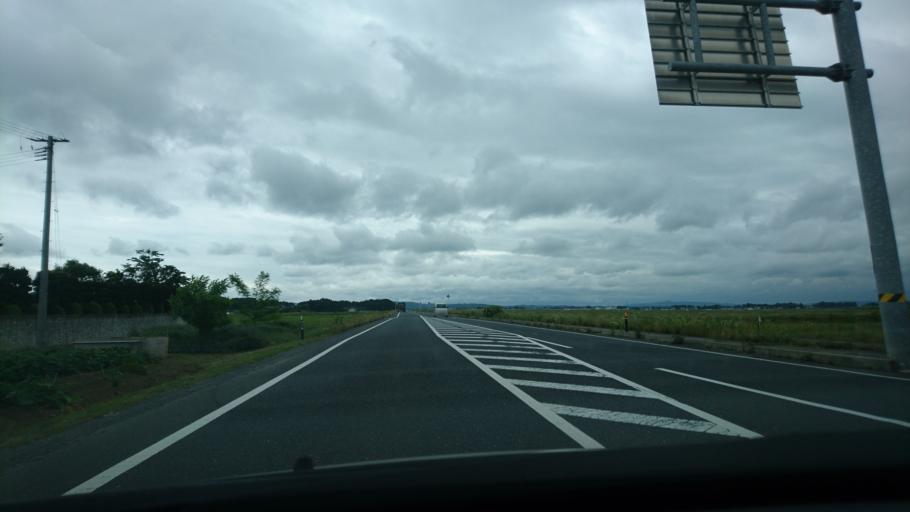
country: JP
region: Miyagi
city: Wakuya
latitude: 38.7072
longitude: 141.2601
